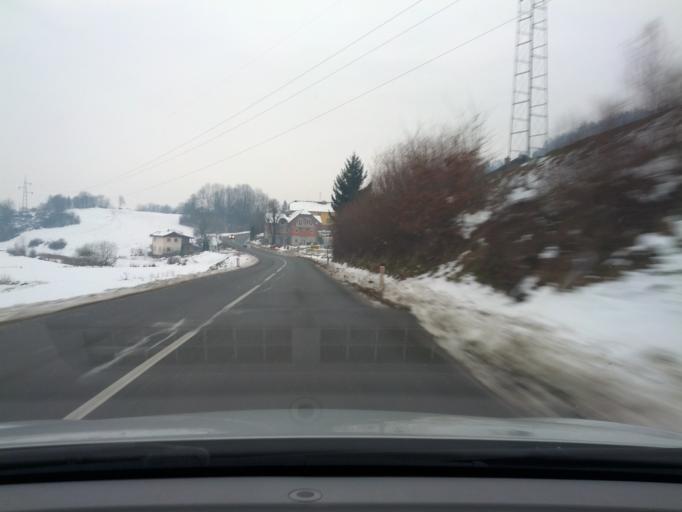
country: SI
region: Lukovica
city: Lukovica pri Domzalah
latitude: 46.1359
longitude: 14.6875
